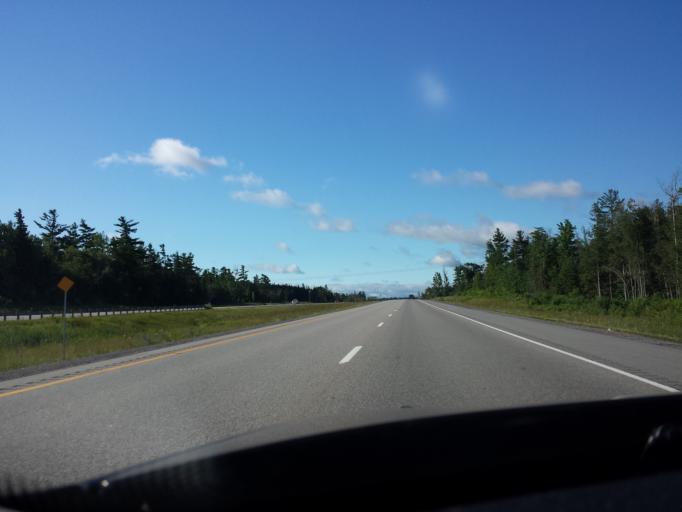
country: CA
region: Ontario
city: Bells Corners
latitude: 45.2631
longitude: -75.9730
